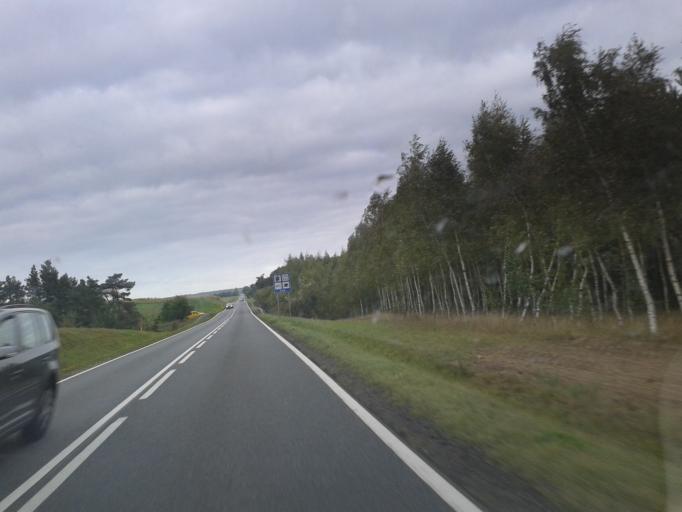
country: PL
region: Kujawsko-Pomorskie
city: Kamien Krajenski
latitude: 53.5110
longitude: 17.5103
